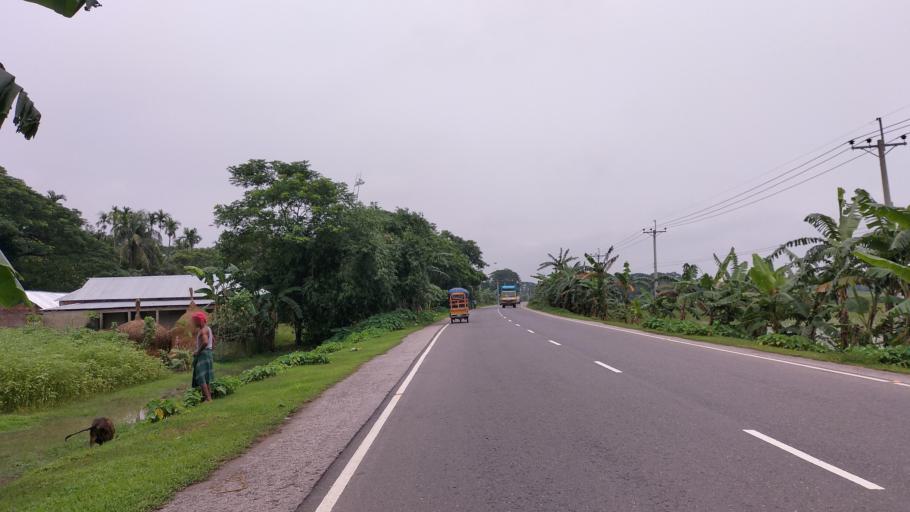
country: BD
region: Dhaka
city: Netrakona
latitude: 24.8522
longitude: 90.6188
